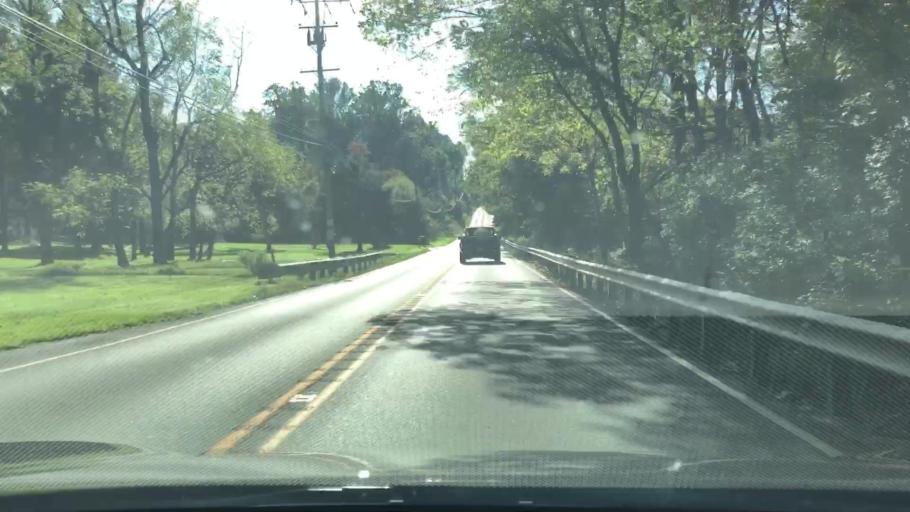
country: US
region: Pennsylvania
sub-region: Chester County
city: West Chester
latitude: 39.9233
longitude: -75.5695
